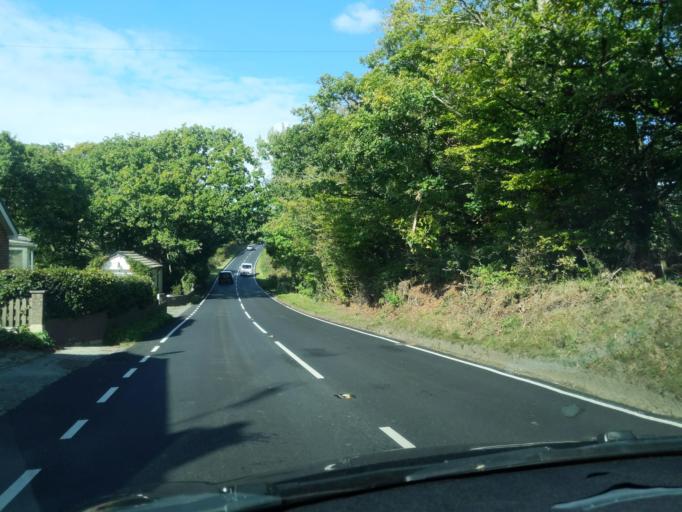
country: GB
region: England
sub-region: Devon
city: Holsworthy
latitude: 50.7989
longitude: -4.3420
